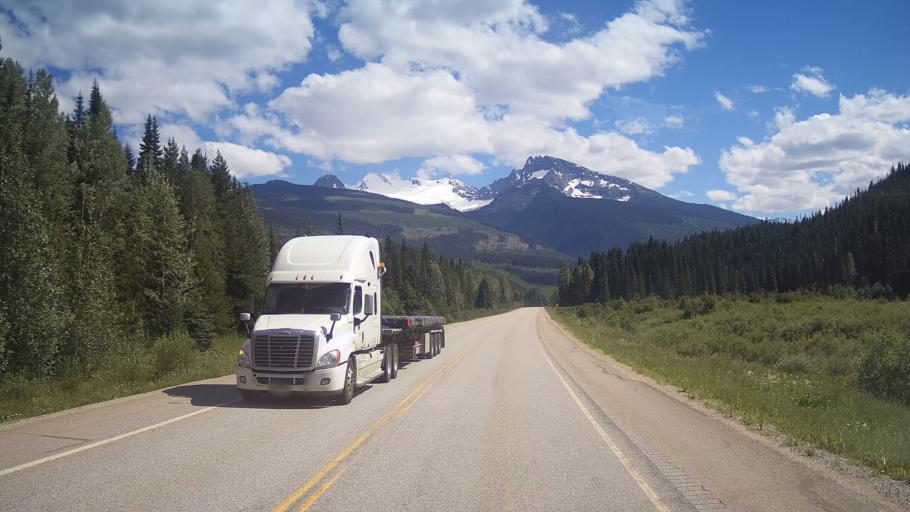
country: CA
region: Alberta
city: Jasper Park Lodge
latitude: 52.5938
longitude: -119.1012
